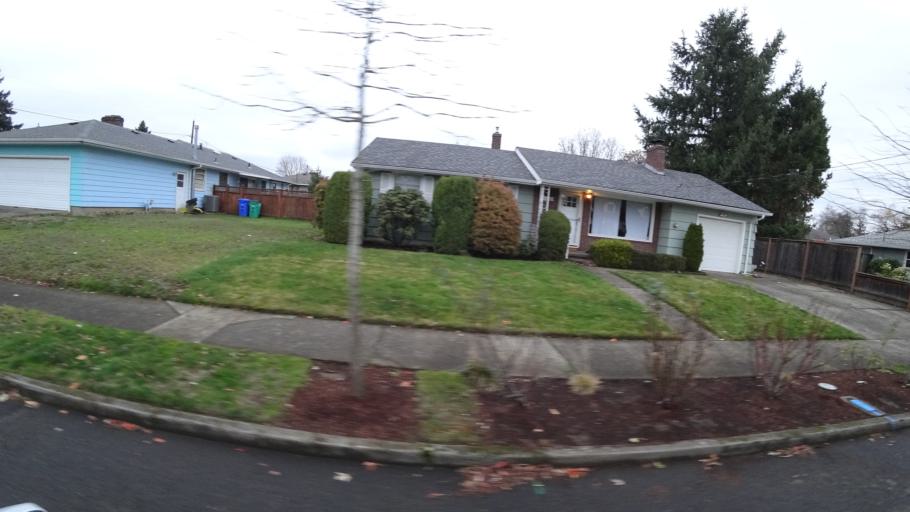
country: US
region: Oregon
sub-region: Multnomah County
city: Lents
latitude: 45.5147
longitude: -122.5360
